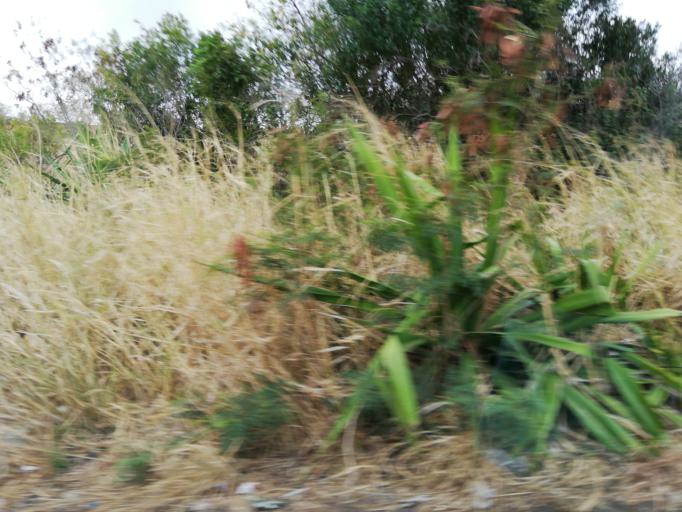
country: MU
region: Black River
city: Petite Riviere
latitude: -20.2089
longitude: 57.4648
